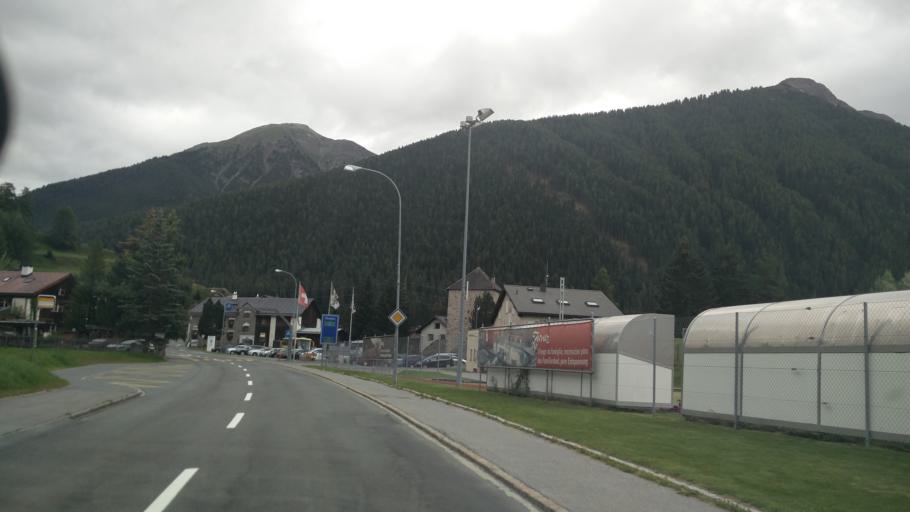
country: CH
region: Grisons
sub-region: Inn District
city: Zernez
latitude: 46.6990
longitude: 10.0960
